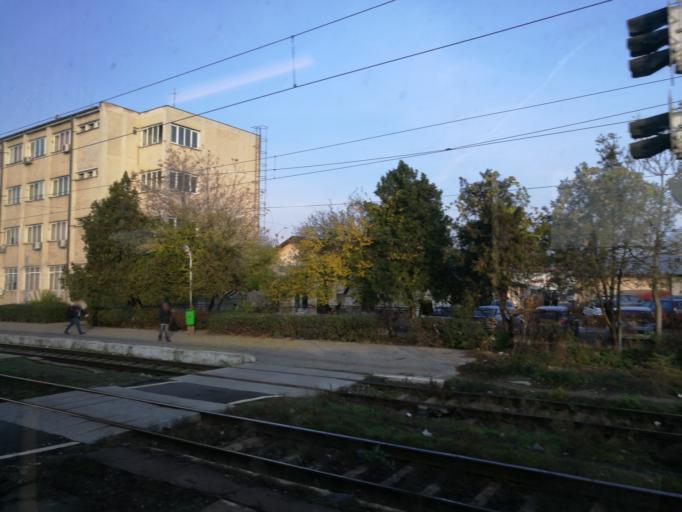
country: RO
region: Buzau
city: Buzau
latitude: 45.1428
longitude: 26.8275
